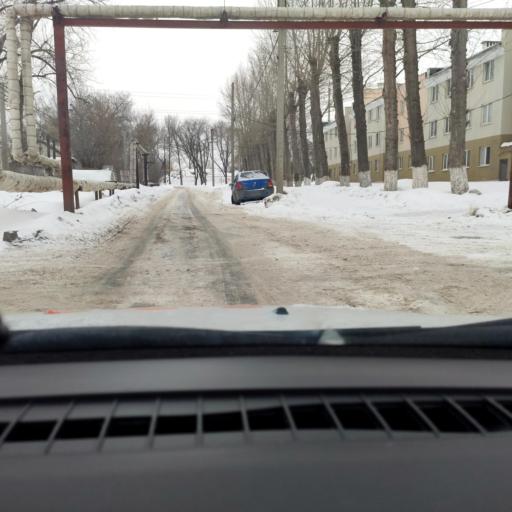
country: RU
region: Samara
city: Novokuybyshevsk
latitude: 53.1143
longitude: 49.9392
